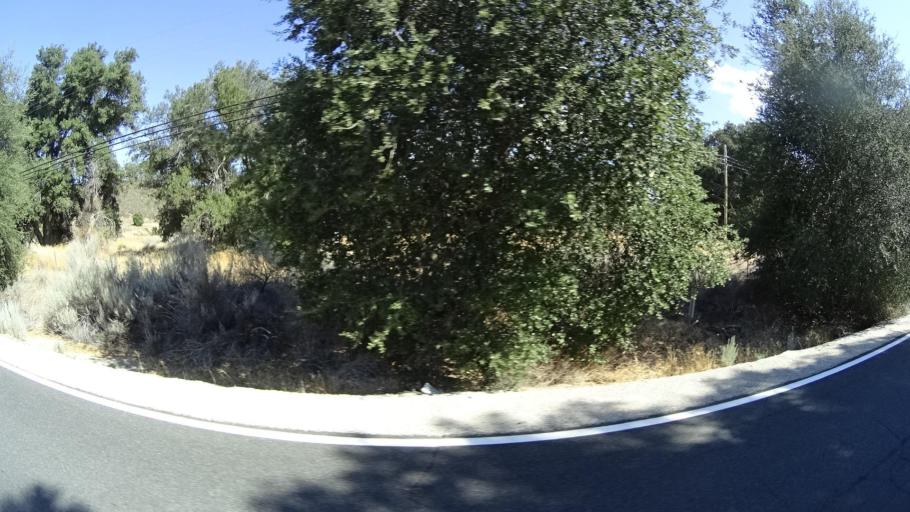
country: US
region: California
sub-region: San Diego County
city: Julian
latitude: 33.2884
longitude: -116.6521
